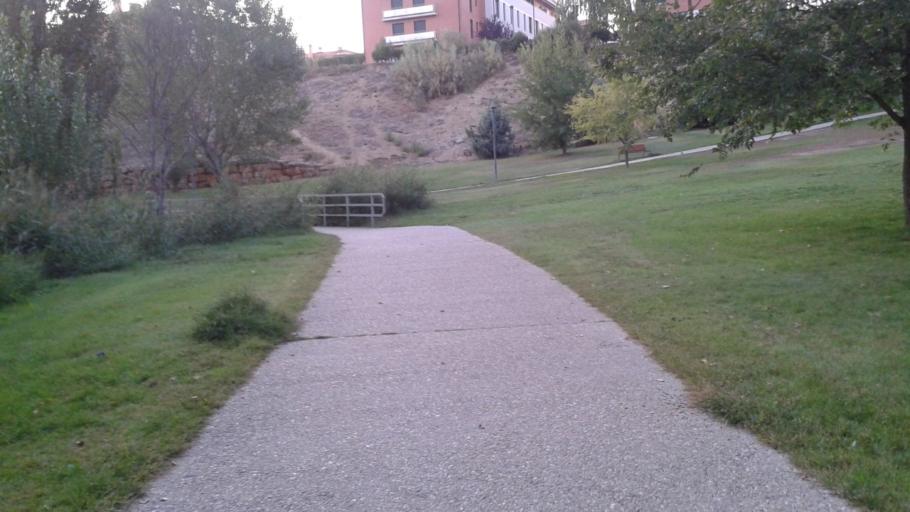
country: ES
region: Castille and Leon
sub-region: Provincia de Valladolid
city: Arroyo
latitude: 41.6088
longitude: -4.7986
